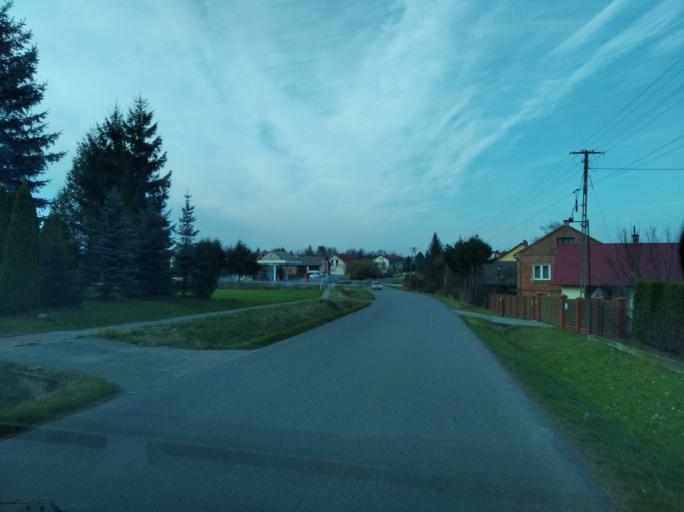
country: PL
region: Subcarpathian Voivodeship
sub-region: Powiat ropczycko-sedziszowski
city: Iwierzyce
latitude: 50.0095
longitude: 21.7553
